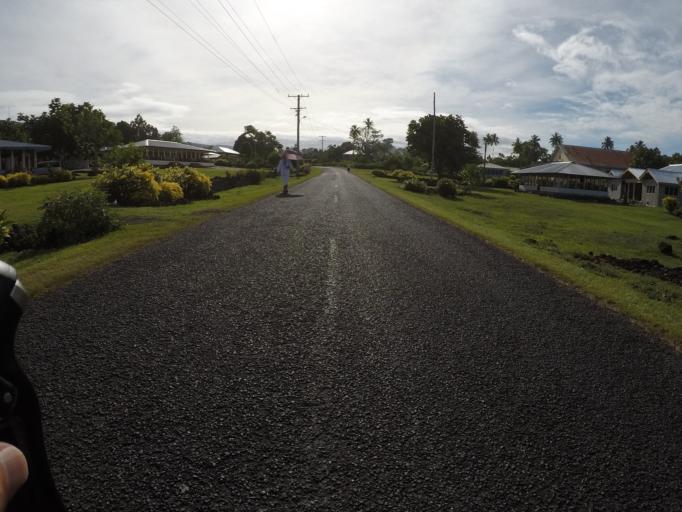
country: WS
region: Vaisigano
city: Asau
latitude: -13.6781
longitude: -172.6338
